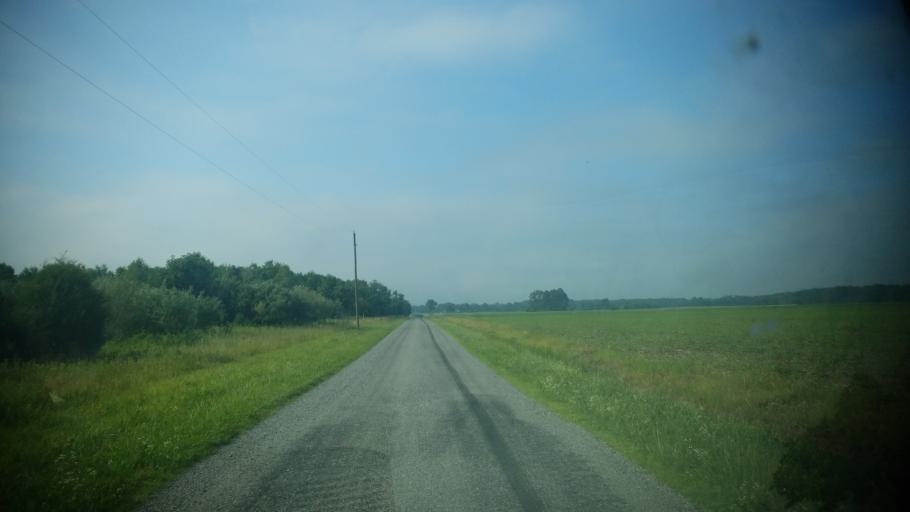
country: US
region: Illinois
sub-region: Clay County
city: Flora
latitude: 38.5949
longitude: -88.3643
